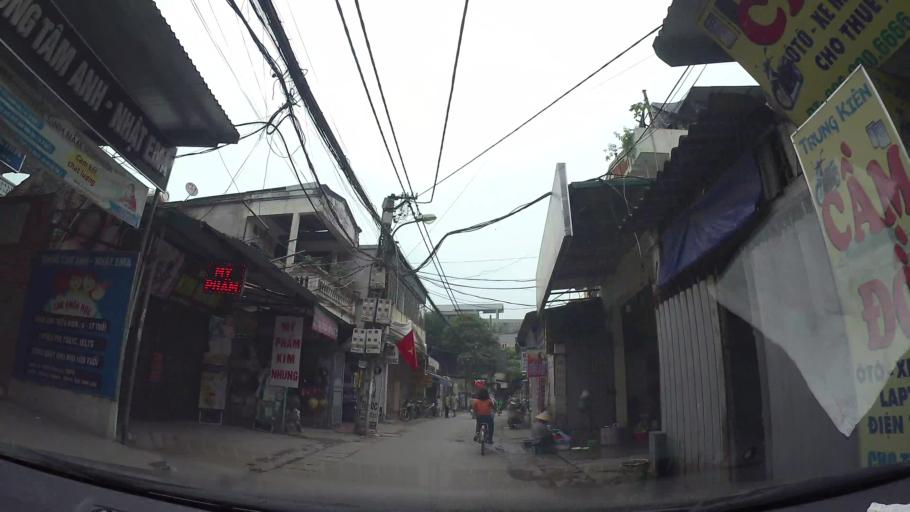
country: VN
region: Ha Noi
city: Hai BaTrung
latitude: 20.9823
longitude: 105.8866
